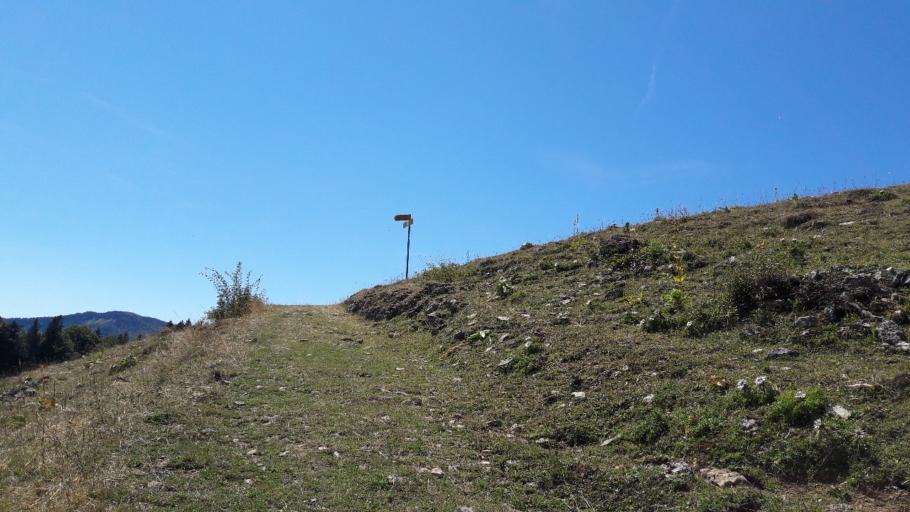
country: CH
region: Solothurn
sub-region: Bezirk Thal
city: Welschenrohr
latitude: 47.2950
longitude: 7.5351
